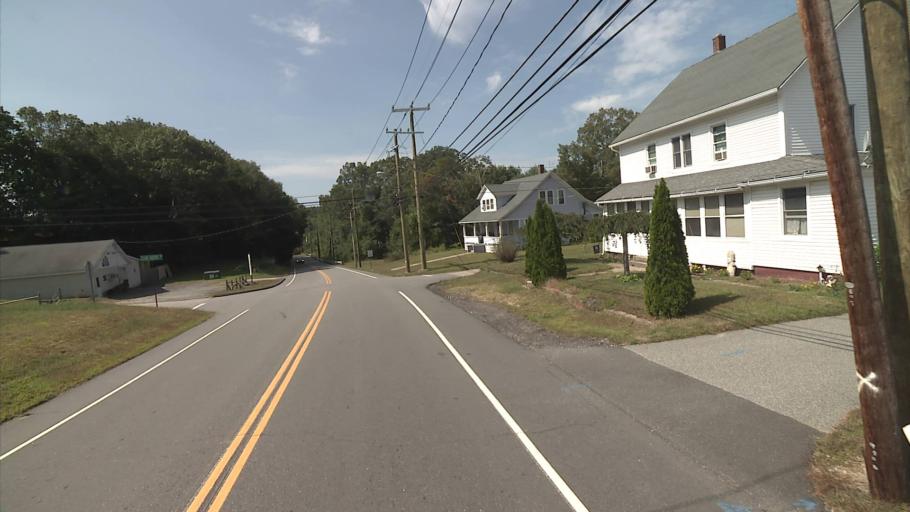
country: US
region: Connecticut
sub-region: New London County
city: Lisbon
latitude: 41.5677
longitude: -72.0395
